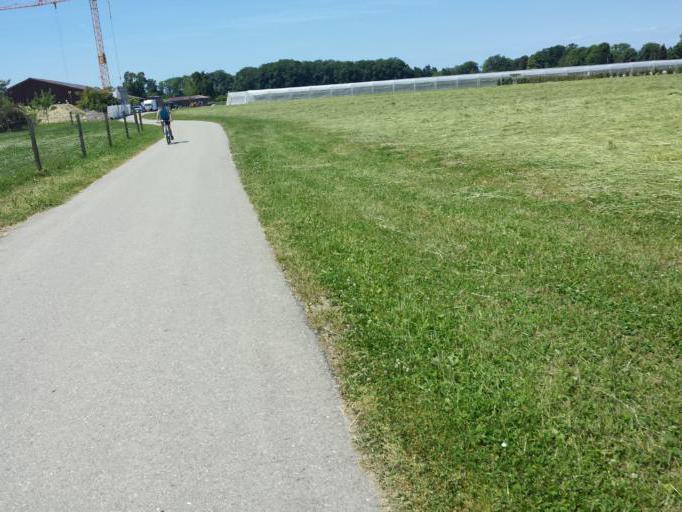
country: CH
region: Thurgau
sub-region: Arbon District
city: Romanshorn
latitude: 47.5753
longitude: 9.3644
